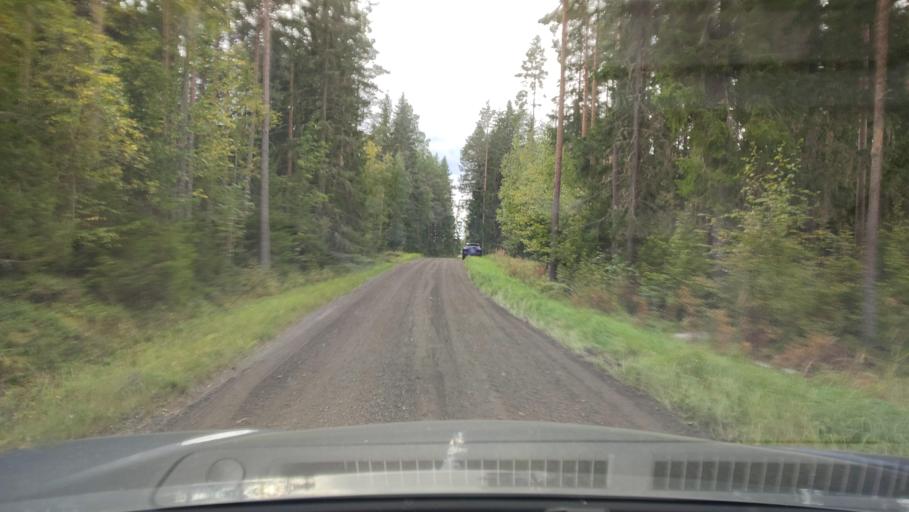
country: FI
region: Southern Ostrobothnia
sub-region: Suupohja
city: Karijoki
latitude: 62.2166
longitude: 21.5686
